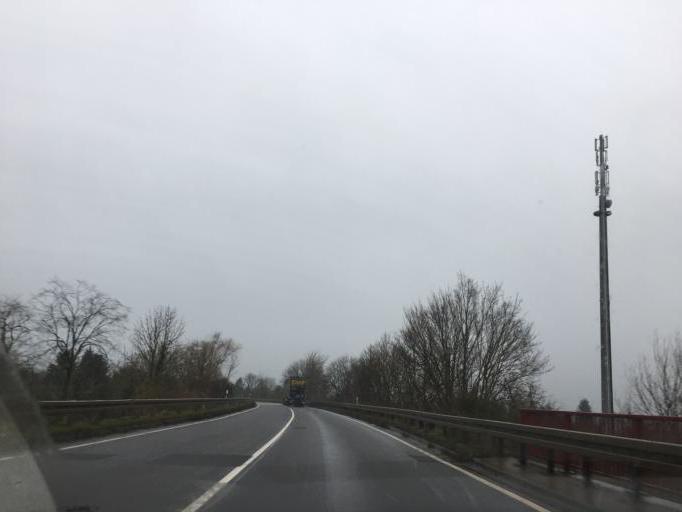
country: DE
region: Saxony-Anhalt
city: Gross Ammensleben
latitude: 52.2357
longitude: 11.5240
